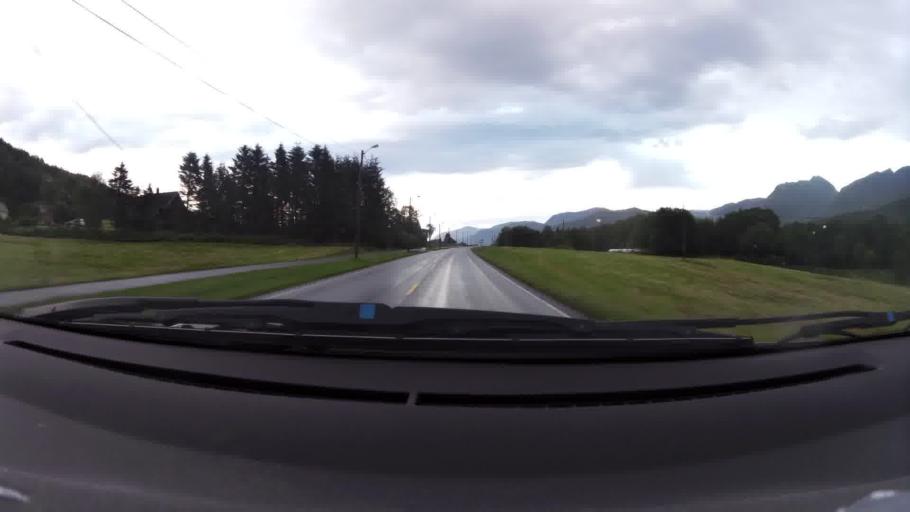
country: NO
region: More og Romsdal
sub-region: Eide
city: Eide
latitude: 62.8927
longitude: 7.3755
